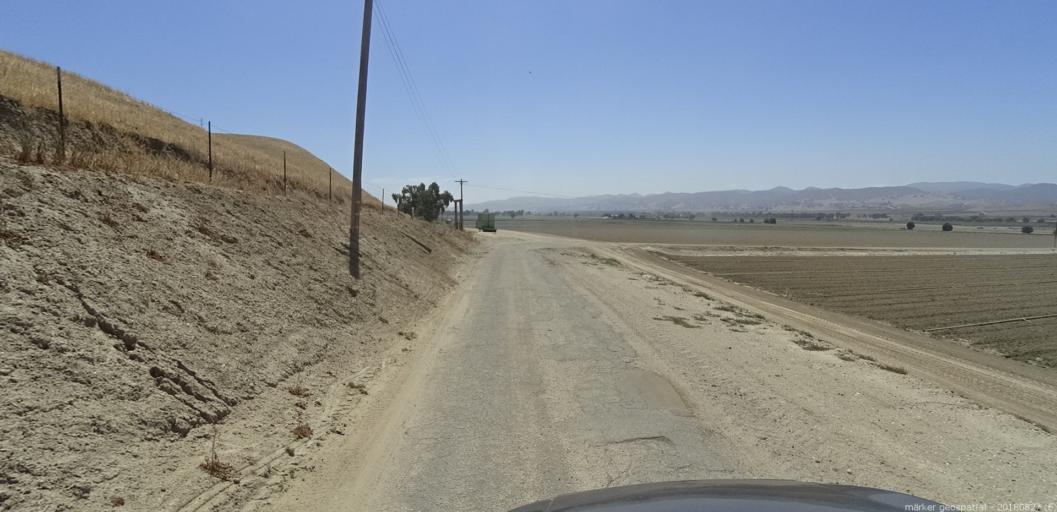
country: US
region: California
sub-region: Monterey County
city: King City
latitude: 36.0469
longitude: -120.9129
